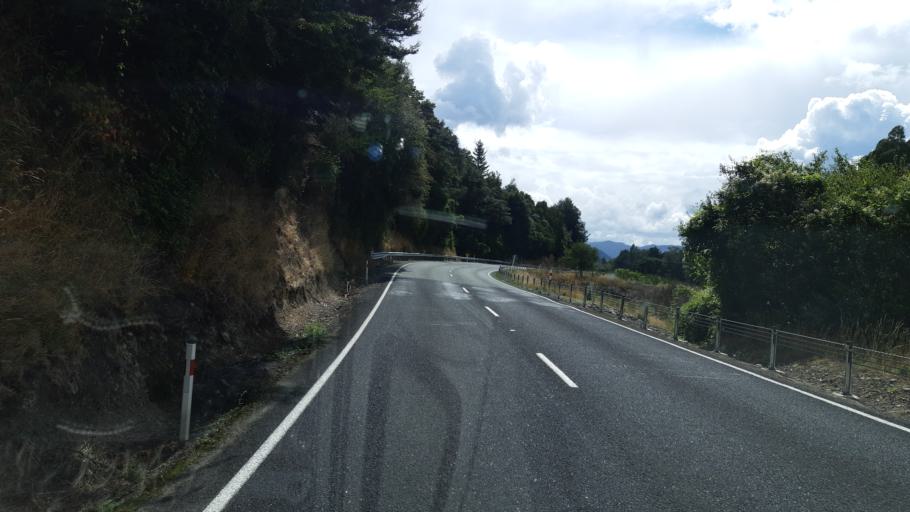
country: NZ
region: Tasman
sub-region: Tasman District
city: Wakefield
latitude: -41.4939
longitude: 172.7969
